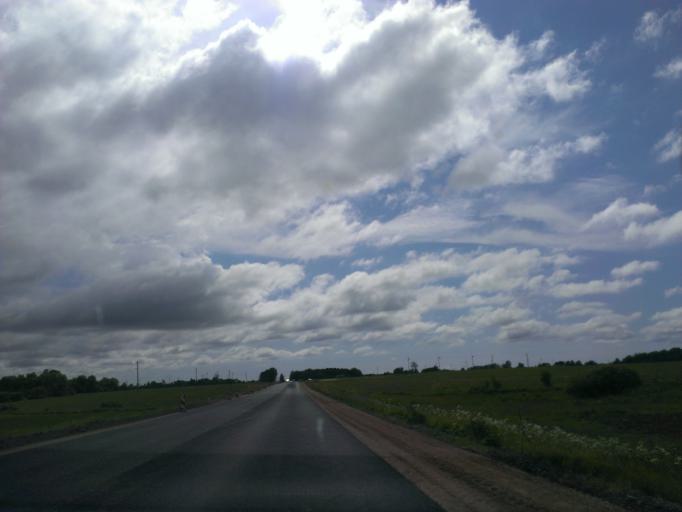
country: LV
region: Durbe
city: Liegi
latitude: 56.5716
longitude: 21.2835
